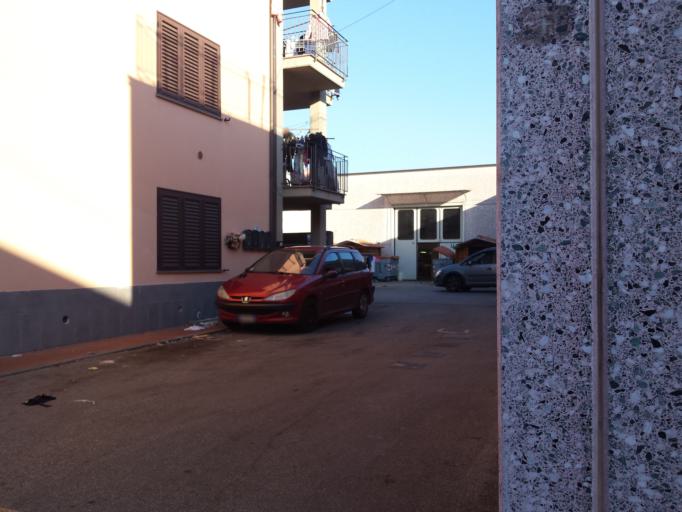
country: IT
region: Tuscany
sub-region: Provincia di Prato
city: Prato
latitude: 43.8857
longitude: 11.0809
